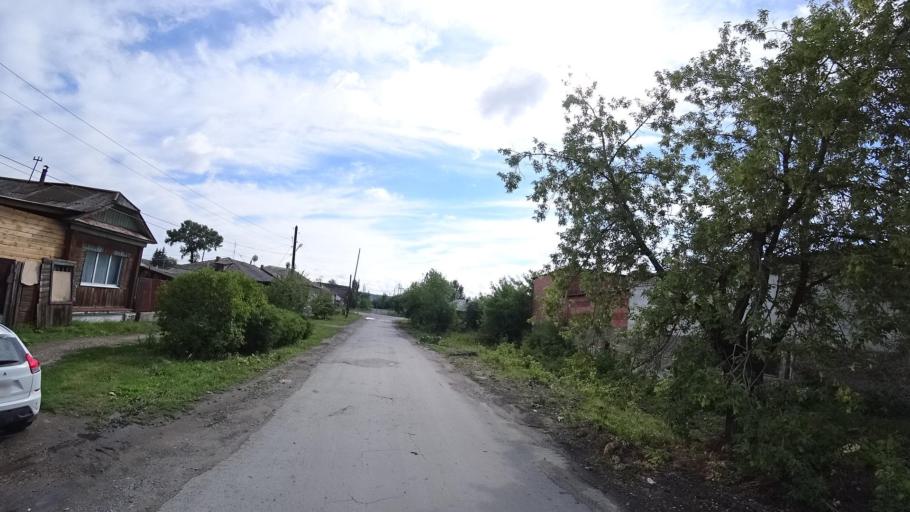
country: RU
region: Sverdlovsk
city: Kamyshlov
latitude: 56.8408
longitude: 62.7086
